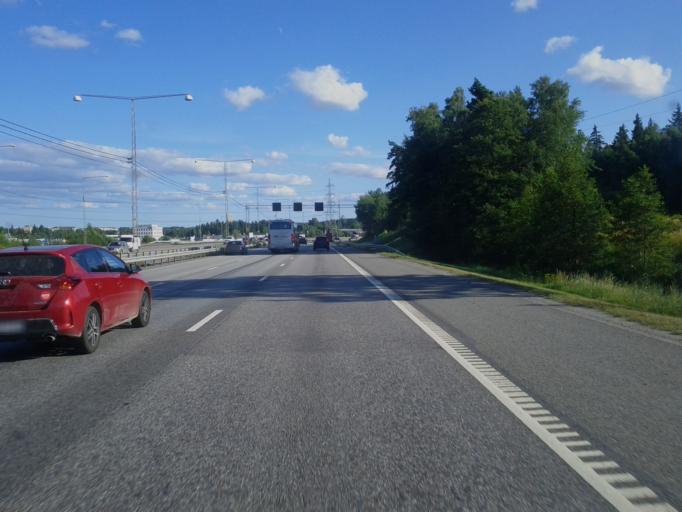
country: SE
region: Stockholm
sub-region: Sollentuna Kommun
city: Sollentuna
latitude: 59.4428
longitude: 17.9219
